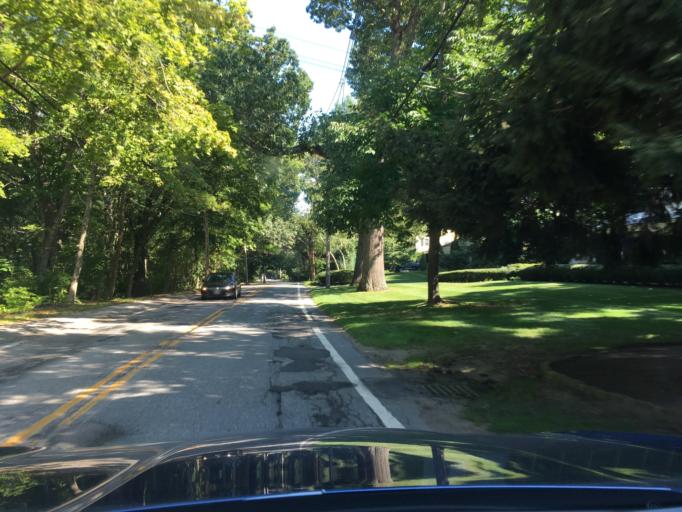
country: US
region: Rhode Island
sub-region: Bristol County
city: Barrington
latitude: 41.7291
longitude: -71.3162
